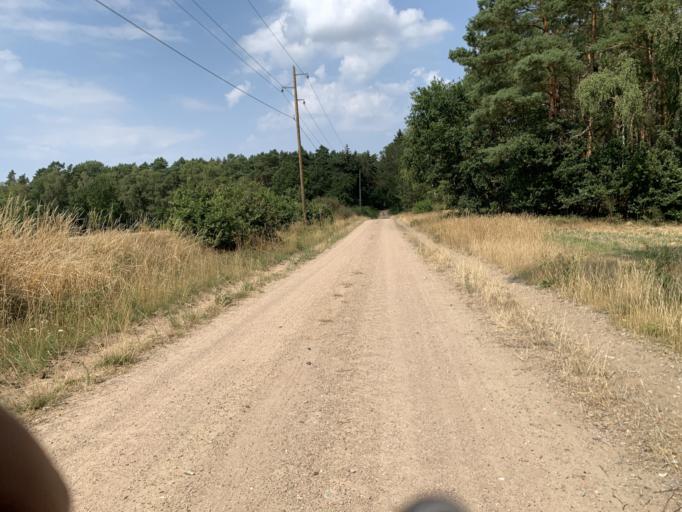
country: DE
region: Lower Saxony
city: Thomasburg
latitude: 53.2042
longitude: 10.6355
